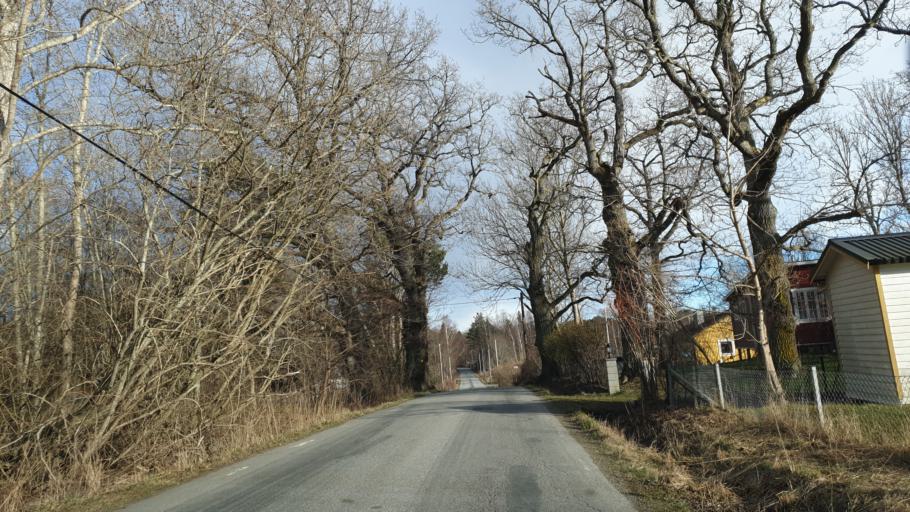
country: SE
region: Stockholm
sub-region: Varmdo Kommun
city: Holo
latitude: 59.3603
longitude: 18.6530
